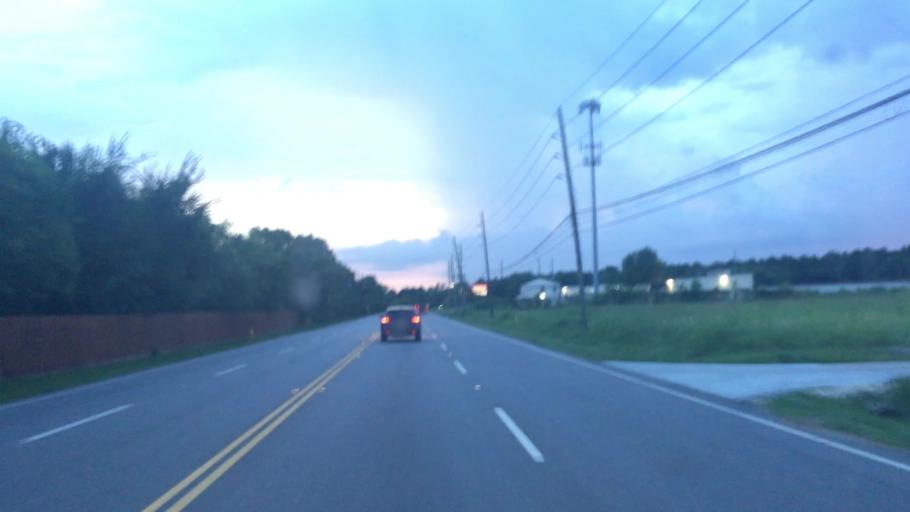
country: US
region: Texas
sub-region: Harris County
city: Humble
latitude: 29.9653
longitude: -95.2405
